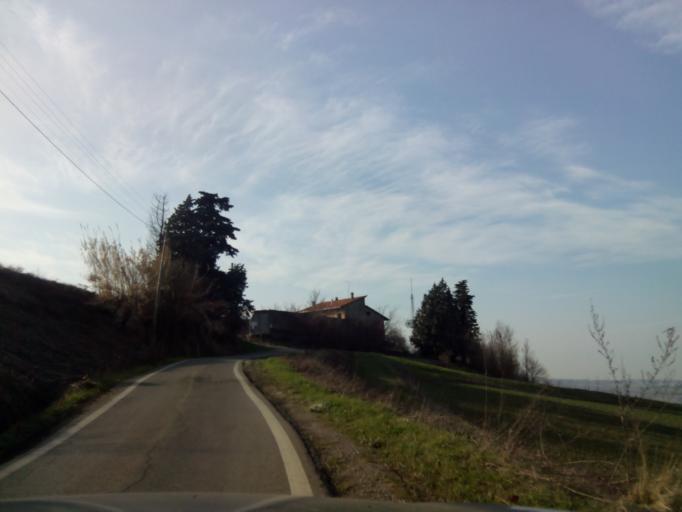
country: IT
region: Emilia-Romagna
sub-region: Provincia di Ravenna
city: Riolo Terme
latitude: 44.3110
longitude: 11.6858
